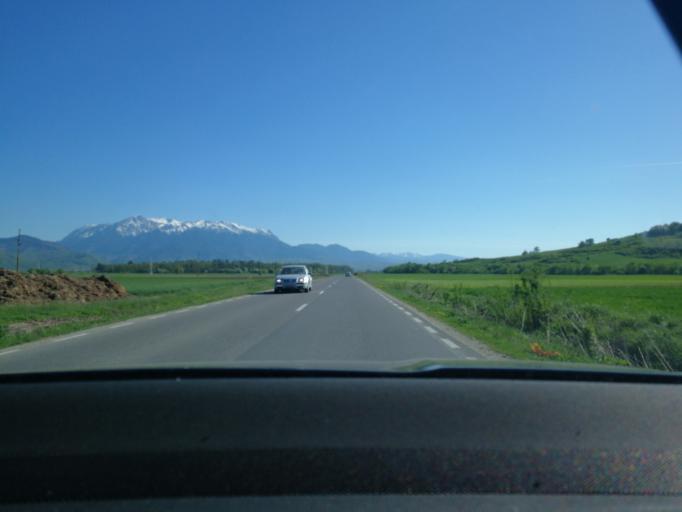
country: RO
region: Brasov
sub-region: Comuna Vulcan
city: Vulcan
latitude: 45.6081
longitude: 25.4219
